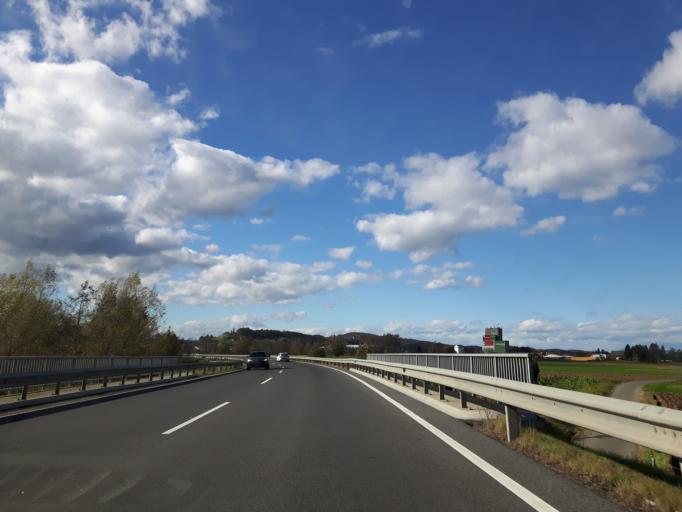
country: AT
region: Styria
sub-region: Politischer Bezirk Suedoststeiermark
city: Feldbach
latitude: 46.9587
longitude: 15.8629
